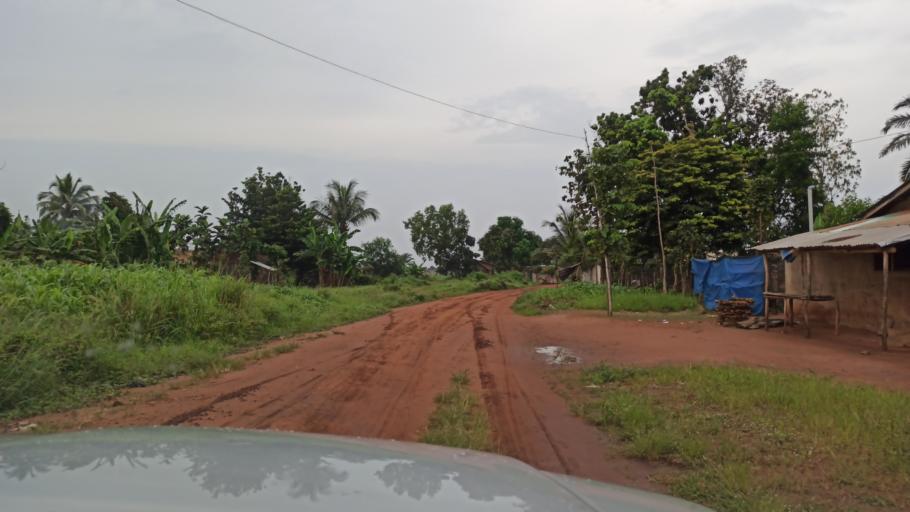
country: BJ
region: Queme
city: Porto-Novo
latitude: 6.4717
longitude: 2.6728
